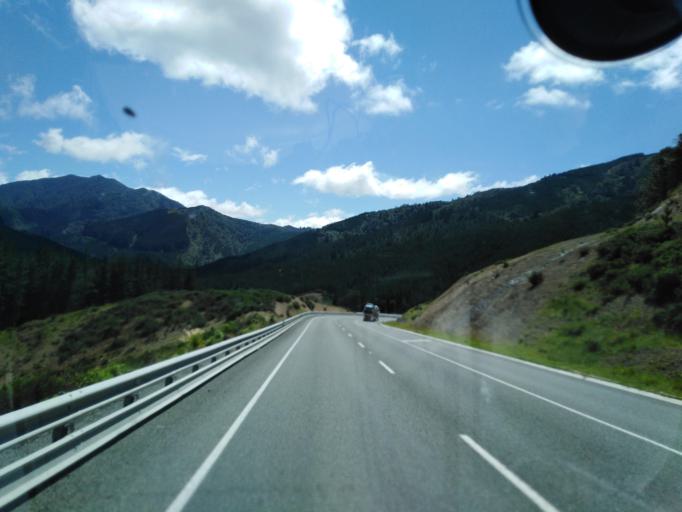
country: NZ
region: Nelson
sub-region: Nelson City
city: Nelson
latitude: -41.1868
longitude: 173.5556
